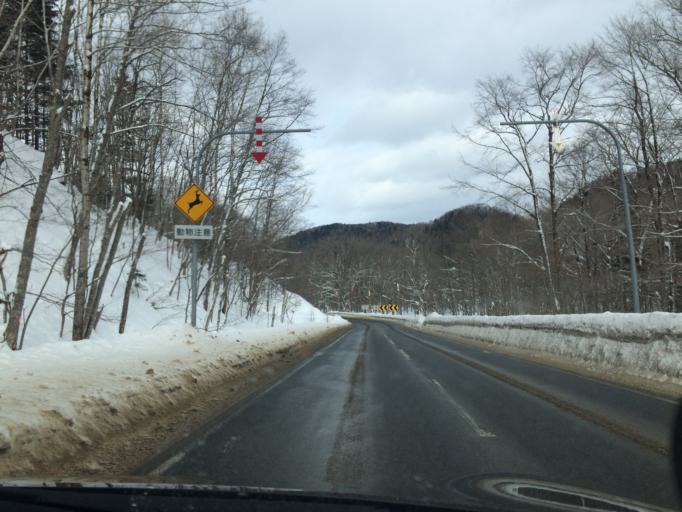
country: JP
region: Hokkaido
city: Shimo-furano
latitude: 42.9191
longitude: 142.3739
